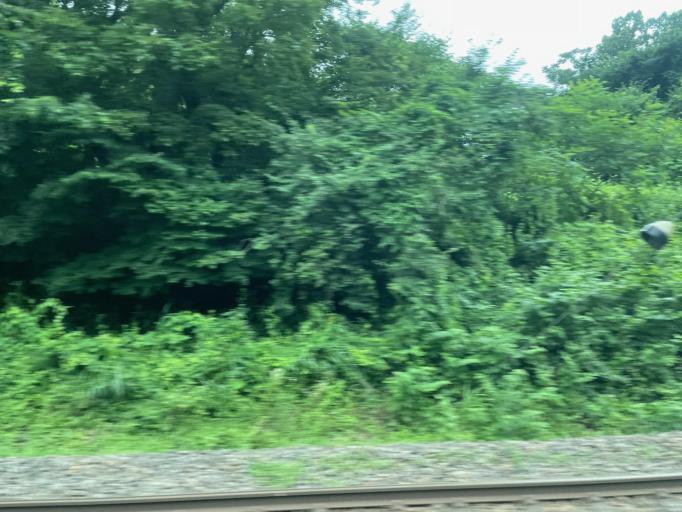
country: JP
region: Tochigi
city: Kuroiso
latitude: 37.0742
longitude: 140.1670
